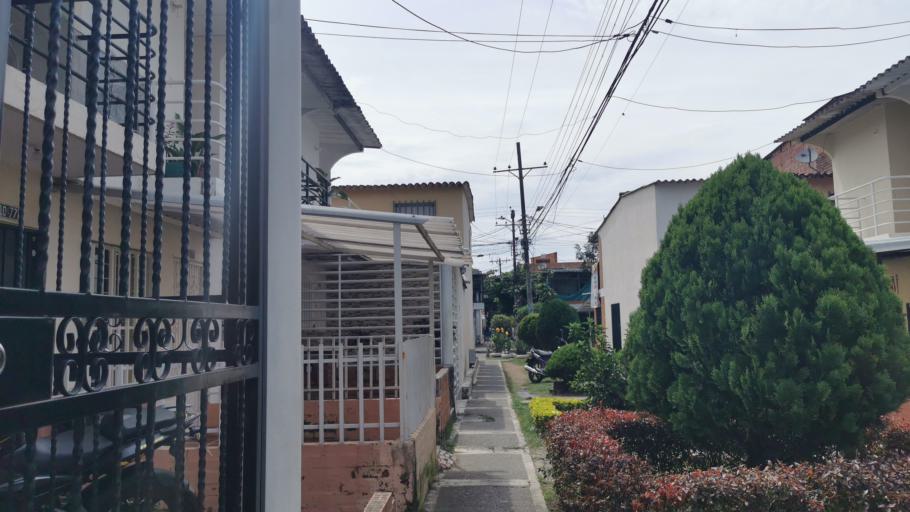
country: CO
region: Valle del Cauca
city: Jamundi
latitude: 3.2515
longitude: -76.5346
